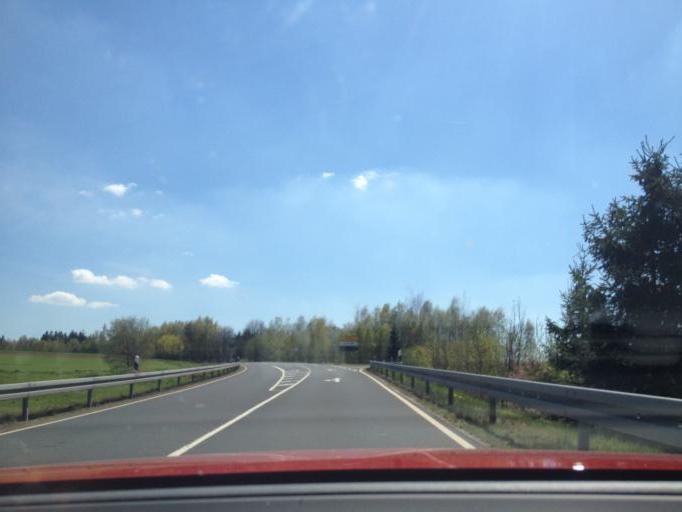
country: DE
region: Bavaria
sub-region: Upper Franconia
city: Kirchenlamitz
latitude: 50.1487
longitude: 11.9590
